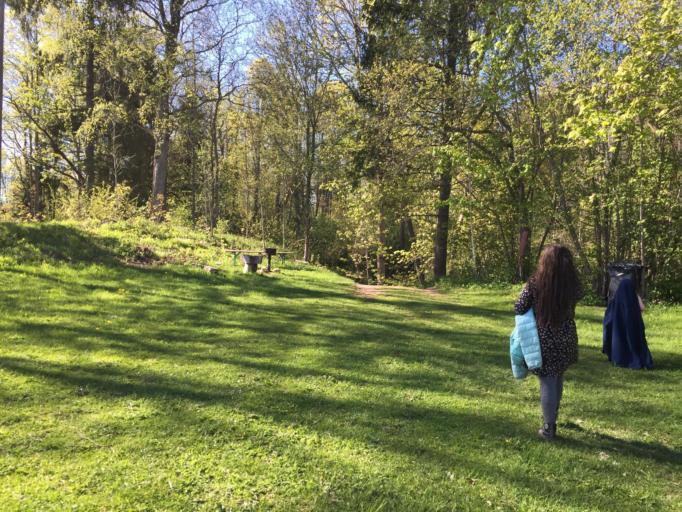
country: LV
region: Madonas Rajons
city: Madona
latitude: 56.8107
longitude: 26.0958
